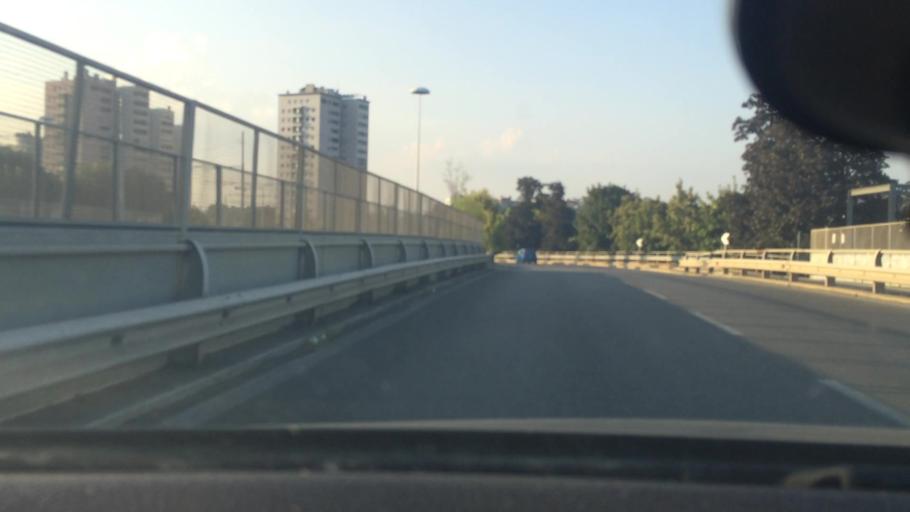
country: IT
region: Lombardy
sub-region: Citta metropolitana di Milano
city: Novate Milanese
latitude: 45.5056
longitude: 9.1407
